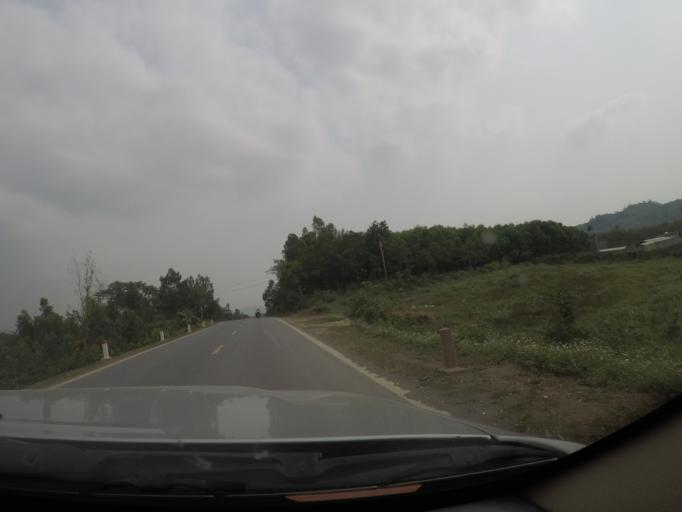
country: VN
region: Thanh Hoa
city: Thi Tran Ben Sung
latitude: 19.3922
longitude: 105.4554
